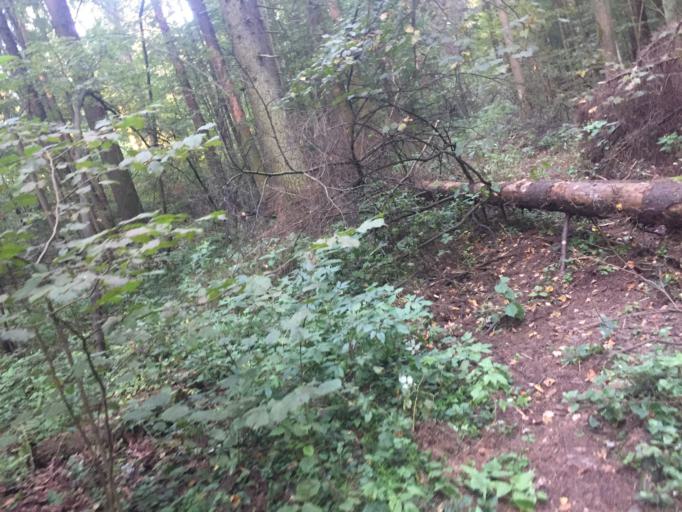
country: RU
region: Moscow
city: Gol'yanovo
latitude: 55.8499
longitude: 37.8160
